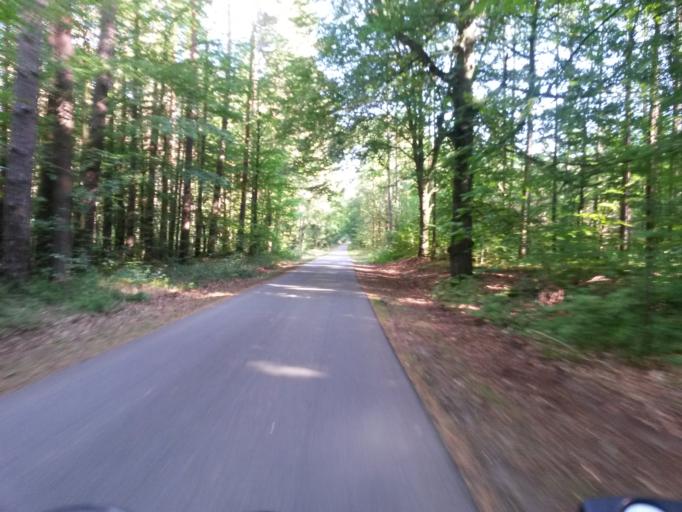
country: DE
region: Brandenburg
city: Templin
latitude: 53.1596
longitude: 13.4381
